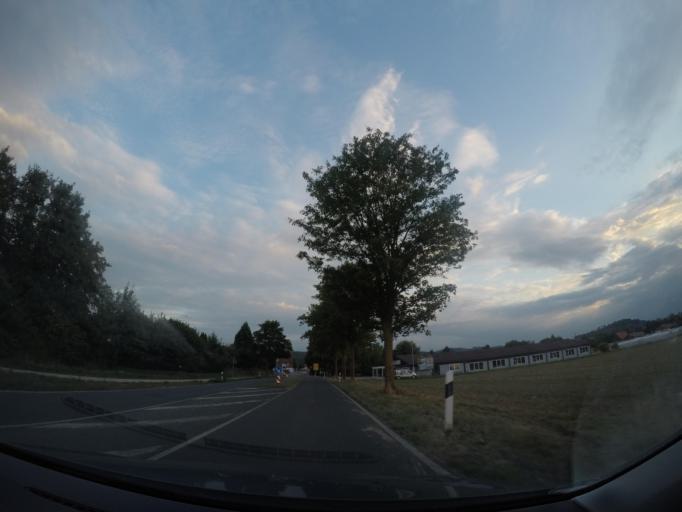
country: DE
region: Lower Saxony
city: Seesen
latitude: 51.8524
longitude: 10.1803
